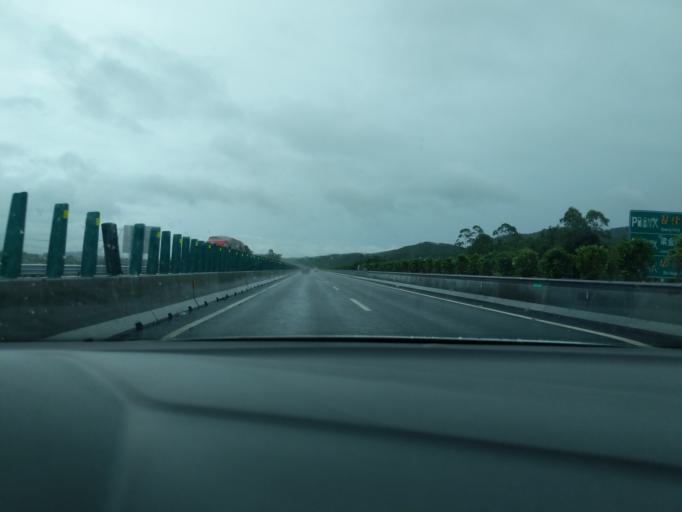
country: CN
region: Guangdong
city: Liangxi
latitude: 22.2679
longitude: 112.3239
